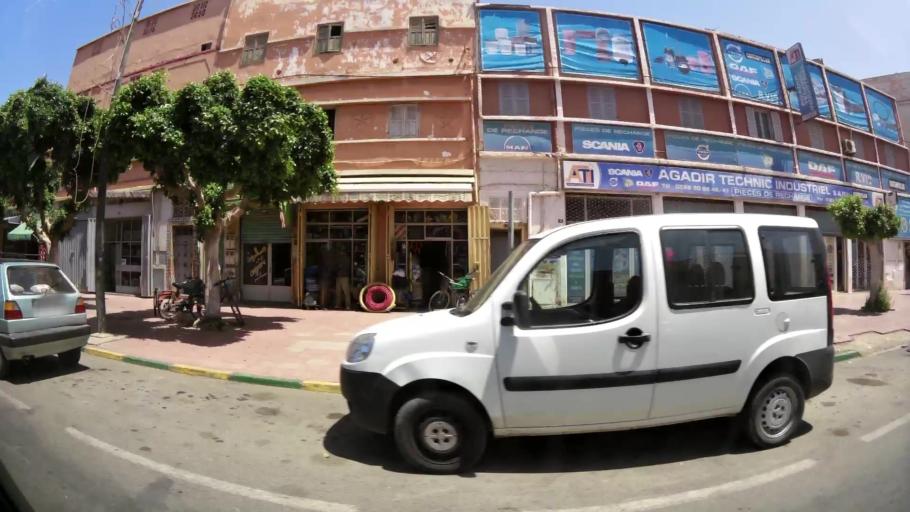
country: MA
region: Souss-Massa-Draa
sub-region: Inezgane-Ait Mellou
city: Inezgane
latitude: 30.3432
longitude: -9.4985
